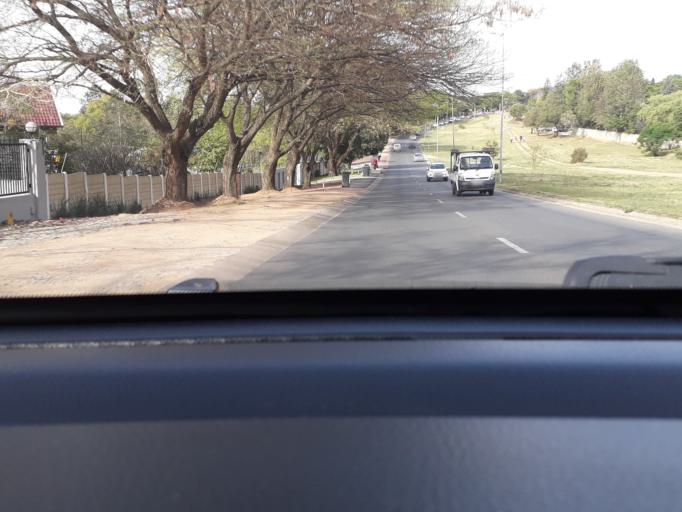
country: ZA
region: Gauteng
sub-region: City of Johannesburg Metropolitan Municipality
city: Diepsloot
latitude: -26.0353
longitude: 28.0012
